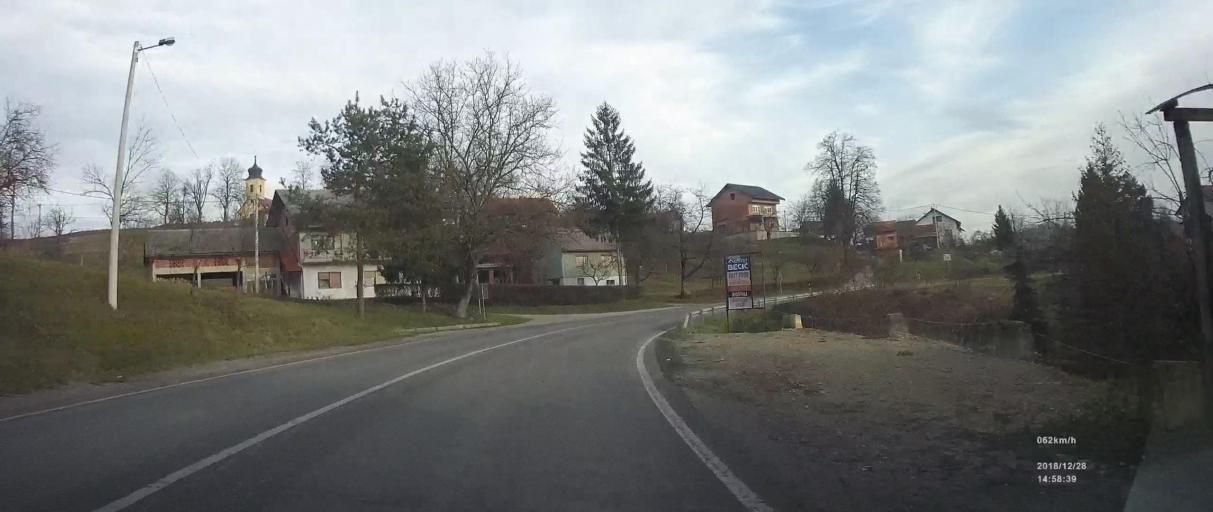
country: HR
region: Karlovacka
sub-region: Grad Karlovac
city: Karlovac
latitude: 45.4577
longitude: 15.4724
